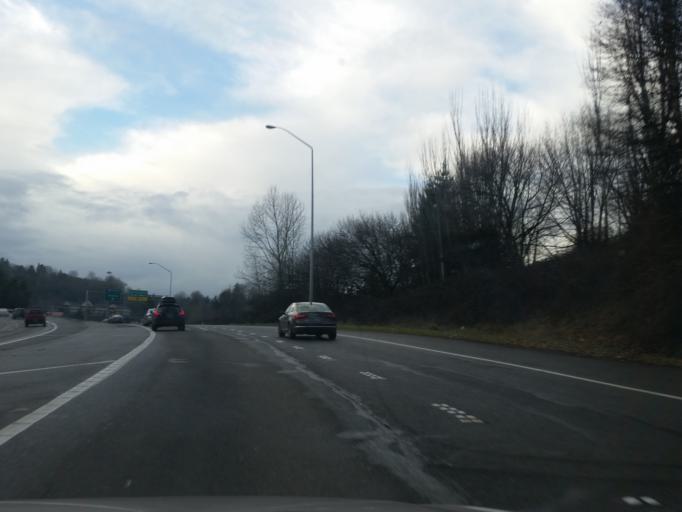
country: US
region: Washington
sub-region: King County
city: Tukwila
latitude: 47.4635
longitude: -122.2605
